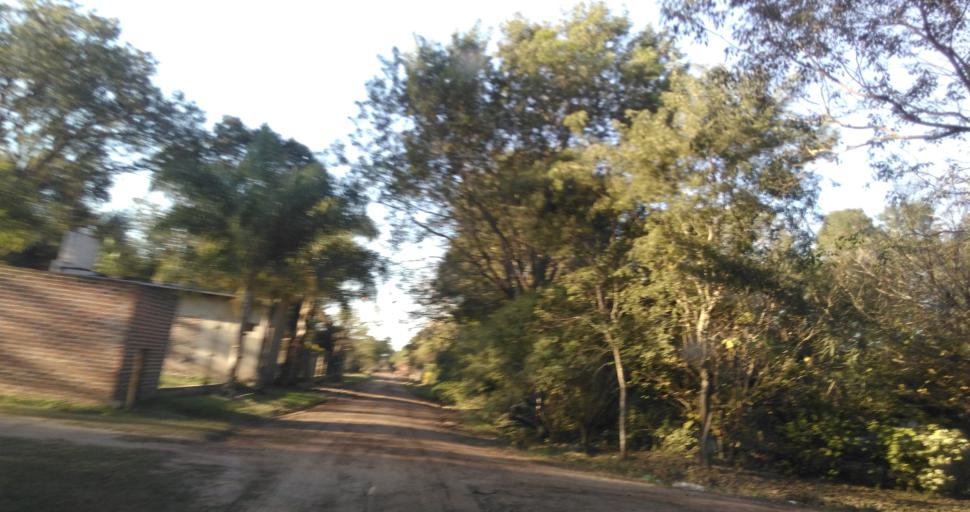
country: AR
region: Chaco
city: Colonia Benitez
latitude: -27.3296
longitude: -58.9566
